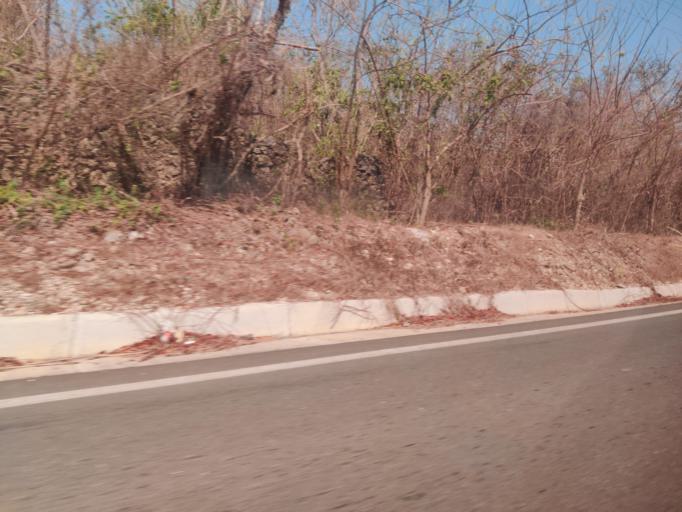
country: CO
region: Bolivar
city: Turbana
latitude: 10.1755
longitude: -75.6461
